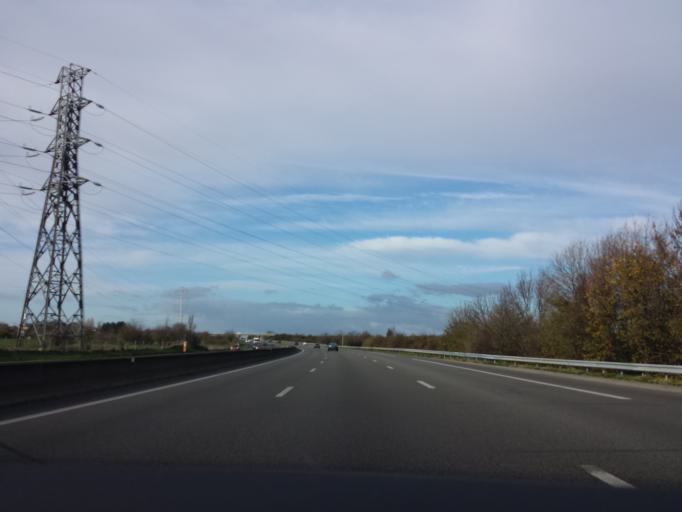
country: FR
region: Ile-de-France
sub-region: Departement des Yvelines
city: Bouafle
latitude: 48.9694
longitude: 1.9149
